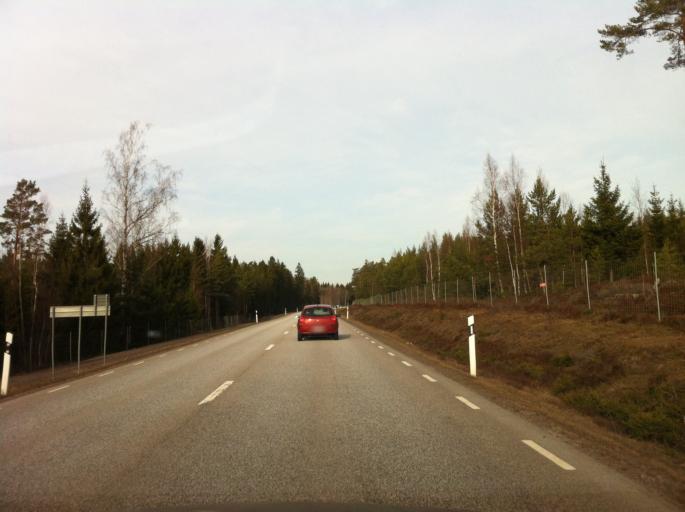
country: SE
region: Vaestra Goetaland
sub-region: Gullspangs Kommun
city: Gullspang
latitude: 58.9143
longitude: 14.0264
